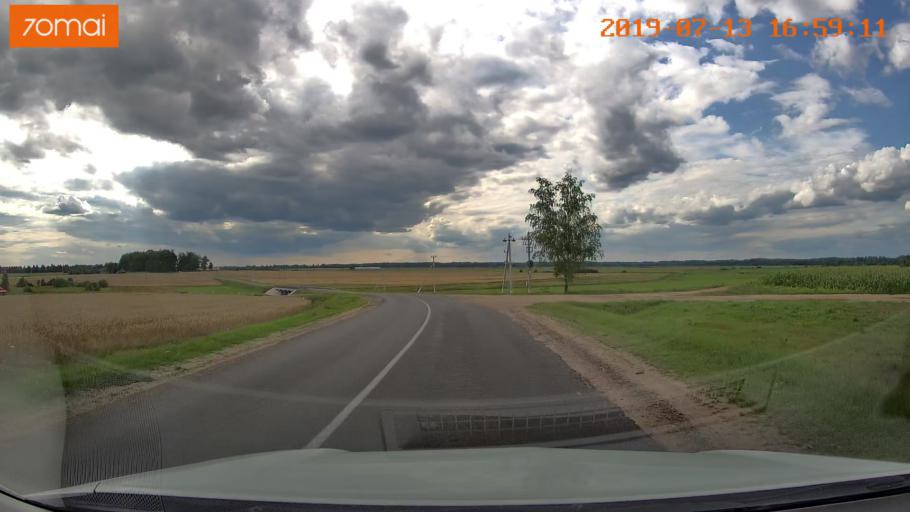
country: BY
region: Mogilev
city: Kirawsk
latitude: 53.2975
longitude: 29.4342
